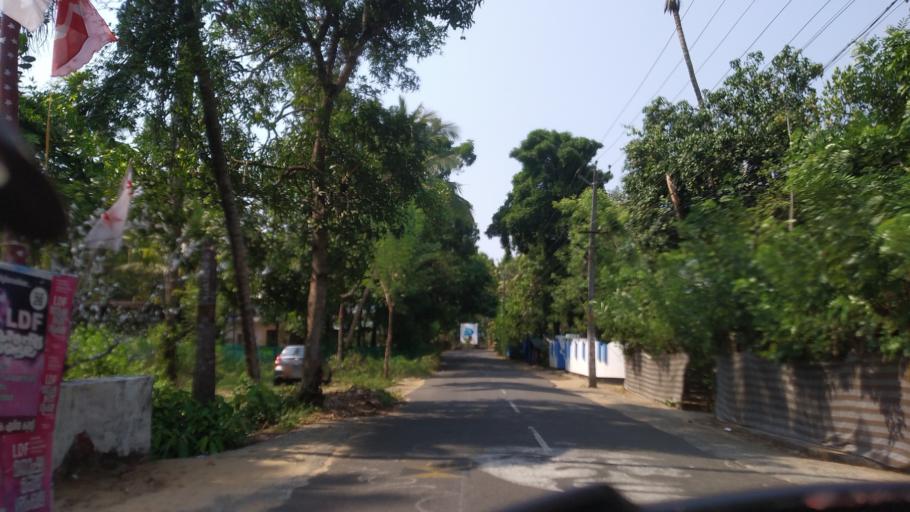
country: IN
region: Kerala
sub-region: Thrissur District
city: Thanniyam
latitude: 10.3441
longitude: 76.1160
